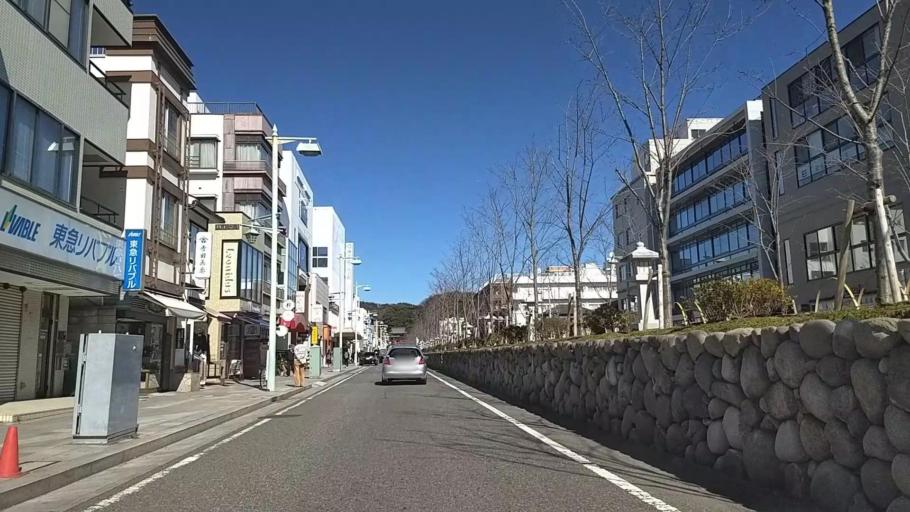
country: JP
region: Kanagawa
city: Kamakura
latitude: 35.3209
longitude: 139.5531
